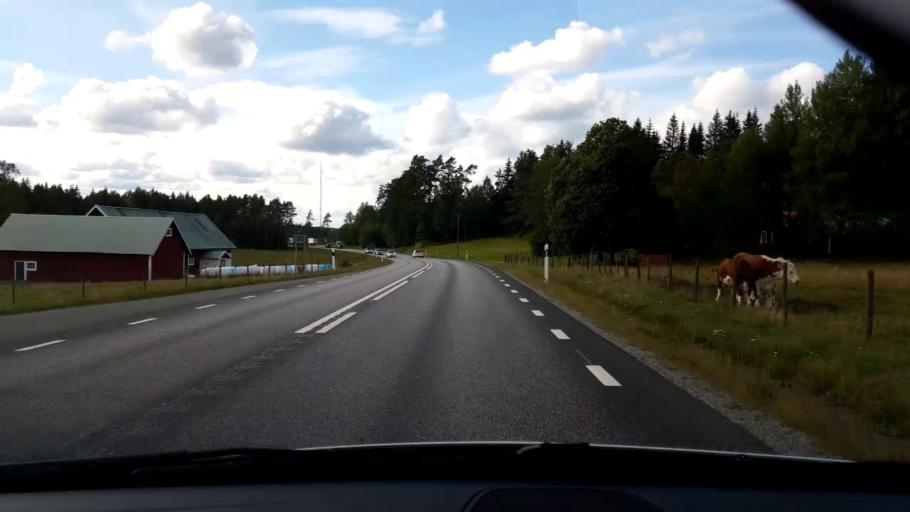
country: SE
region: Joenkoeping
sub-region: Savsjo Kommun
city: Vrigstad
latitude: 57.3636
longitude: 14.4540
